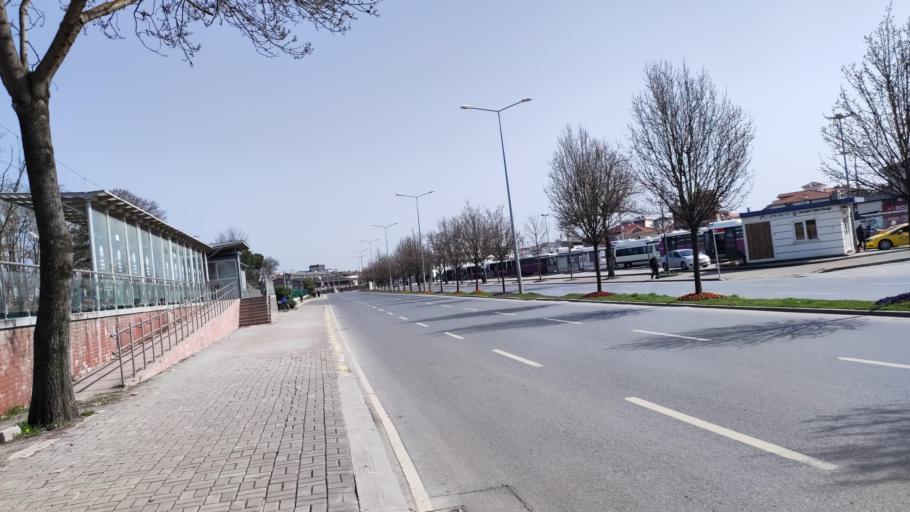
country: TR
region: Sakarya
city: Adapazari
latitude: 40.7706
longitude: 30.3908
